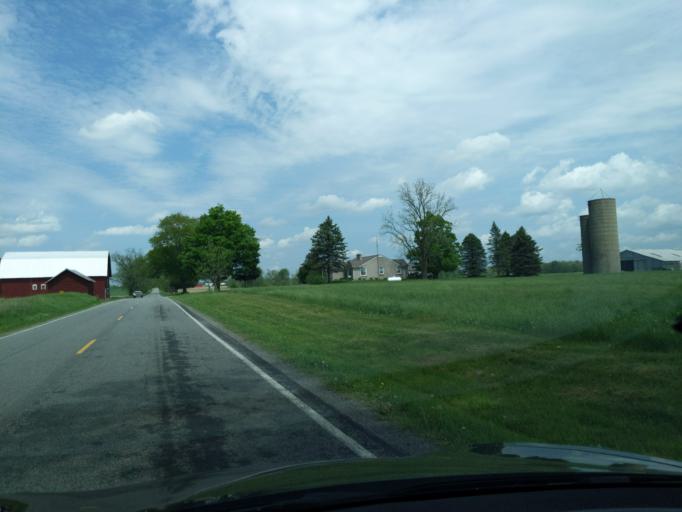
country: US
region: Michigan
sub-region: Ingham County
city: Stockbridge
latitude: 42.4718
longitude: -84.1603
